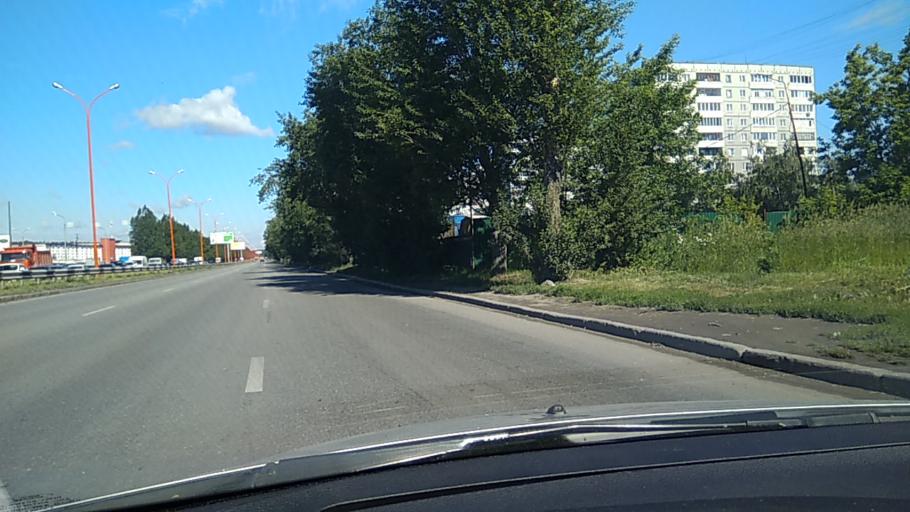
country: RU
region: Sverdlovsk
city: Sovkhoznyy
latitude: 56.7919
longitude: 60.5728
